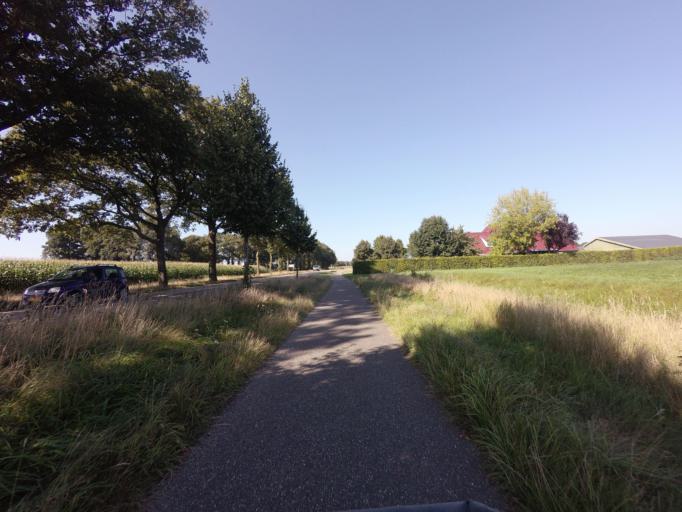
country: NL
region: Overijssel
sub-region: Gemeente Hardenberg
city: Hardenberg
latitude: 52.5306
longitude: 6.5933
